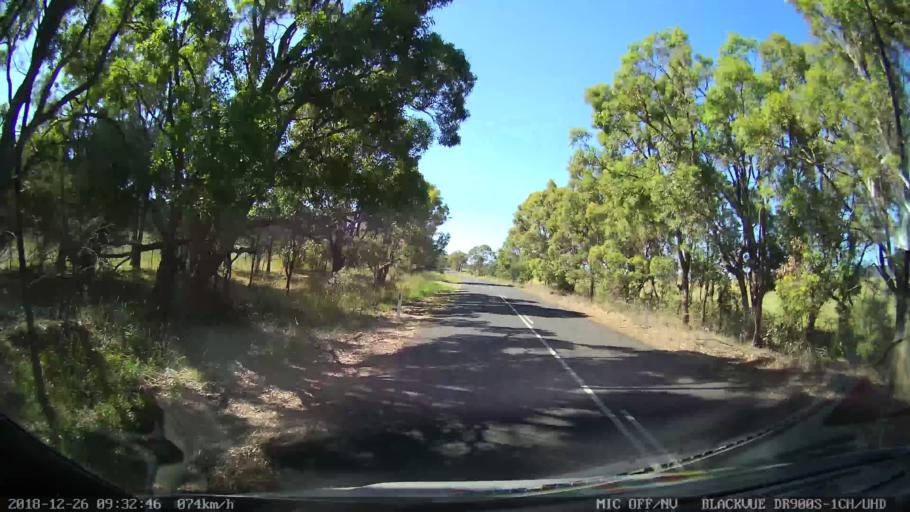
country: AU
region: New South Wales
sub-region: Mid-Western Regional
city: Kandos
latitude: -32.8880
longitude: 150.0330
